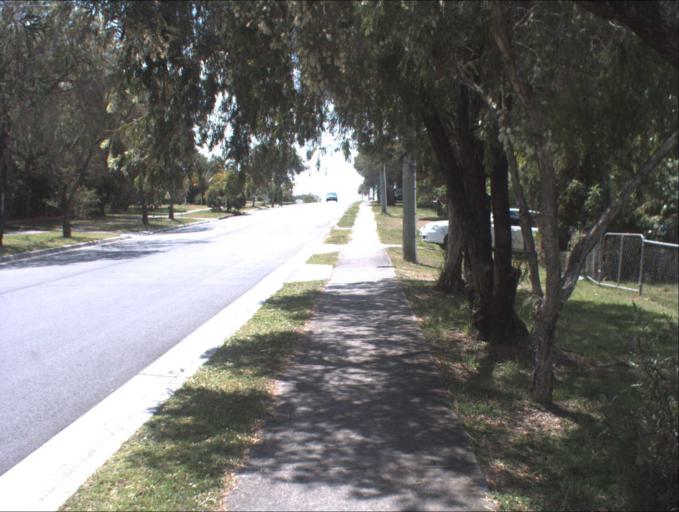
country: AU
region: Queensland
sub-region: Logan
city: Woodridge
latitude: -27.6293
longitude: 153.1023
